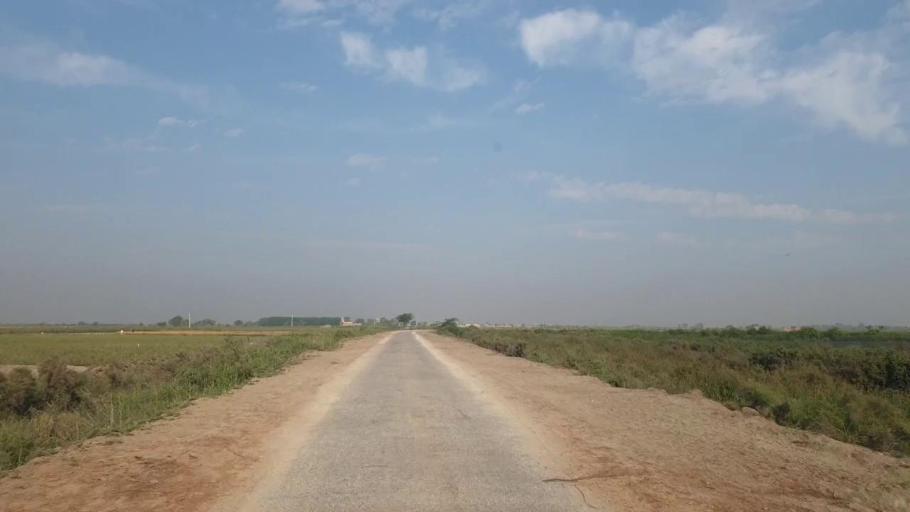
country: PK
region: Sindh
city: Tando Bago
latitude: 24.8519
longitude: 68.9702
